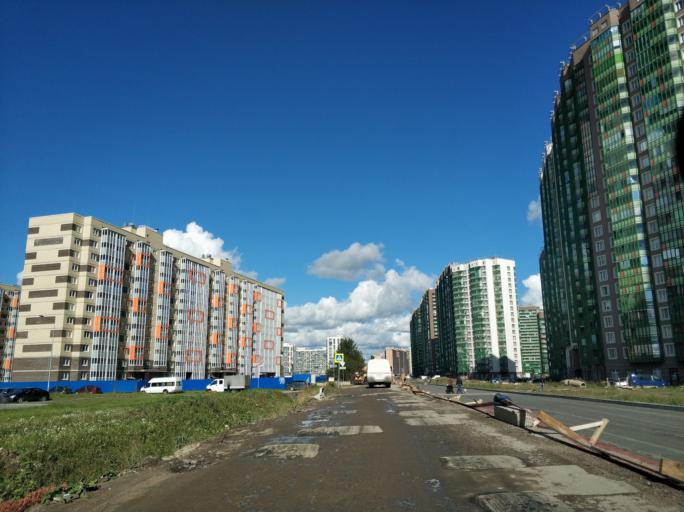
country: RU
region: St.-Petersburg
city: Grazhdanka
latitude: 60.0526
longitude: 30.4197
